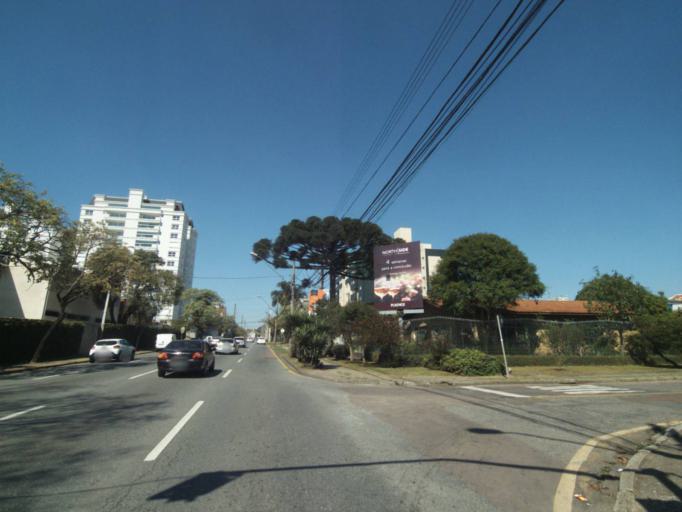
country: BR
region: Parana
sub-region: Curitiba
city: Curitiba
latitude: -25.3962
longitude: -49.2445
